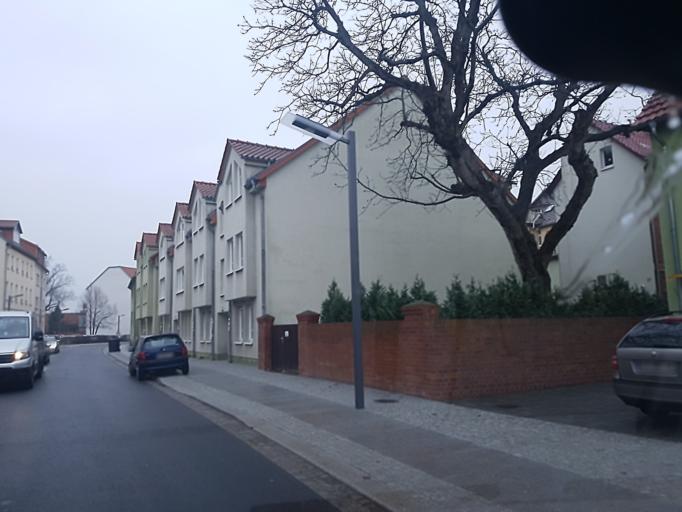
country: DE
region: Brandenburg
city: Finsterwalde
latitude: 51.6301
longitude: 13.7063
